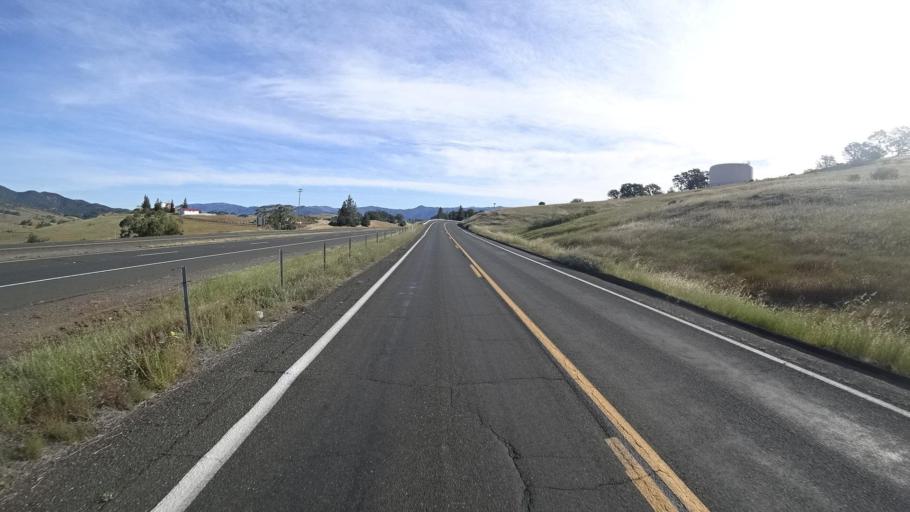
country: US
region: California
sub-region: Lake County
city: North Lakeport
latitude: 39.0982
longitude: -122.9135
